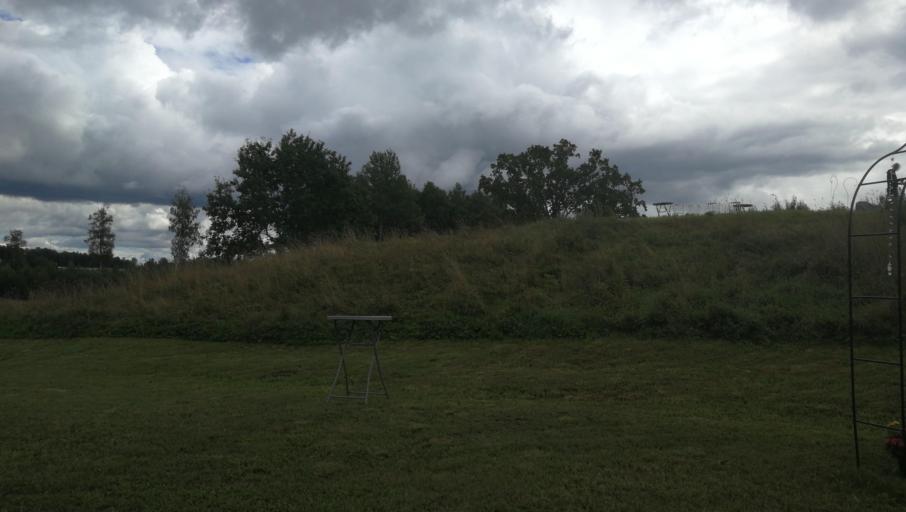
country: LV
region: Seja
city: Loja
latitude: 57.2581
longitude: 24.6316
